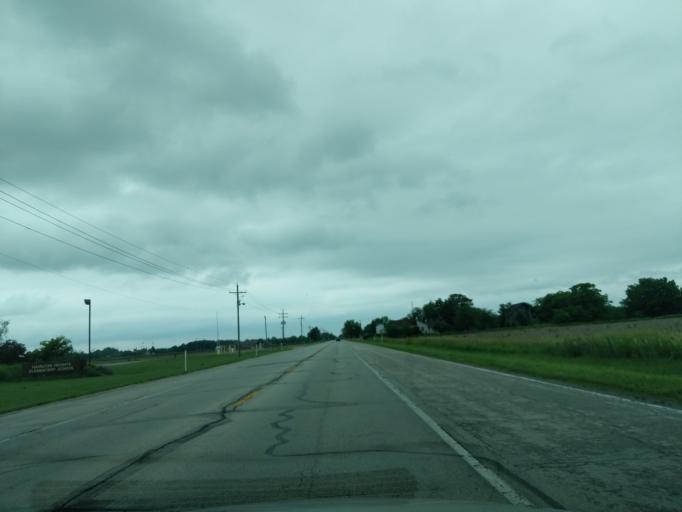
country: US
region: Indiana
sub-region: Hamilton County
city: Arcadia
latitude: 40.1546
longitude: -86.0133
